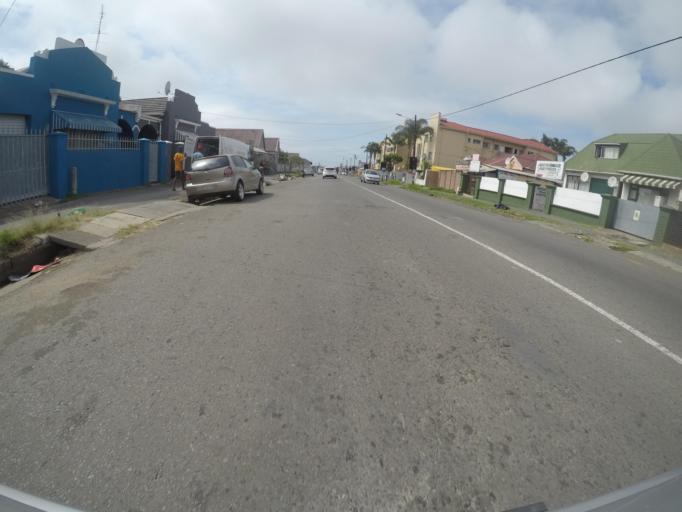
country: ZA
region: Eastern Cape
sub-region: Buffalo City Metropolitan Municipality
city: East London
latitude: -33.0001
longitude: 27.9049
